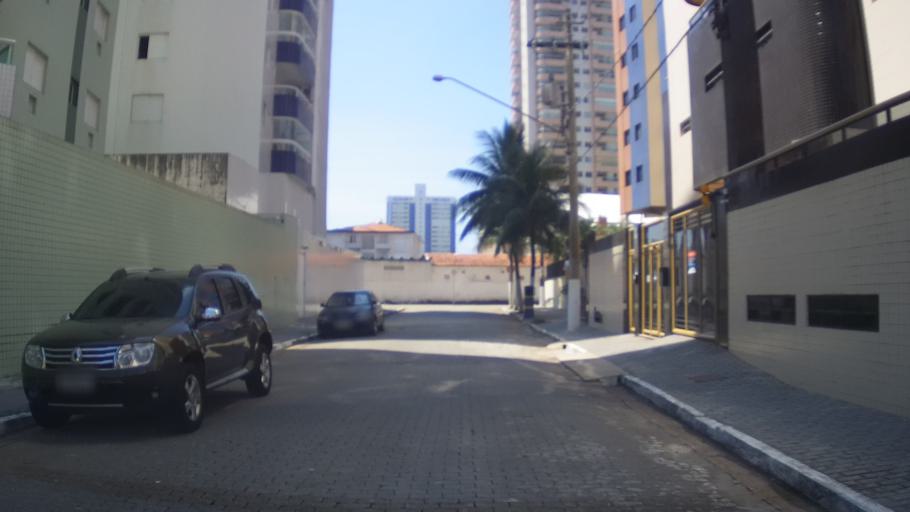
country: BR
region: Sao Paulo
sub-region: Praia Grande
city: Praia Grande
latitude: -24.0166
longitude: -46.4390
